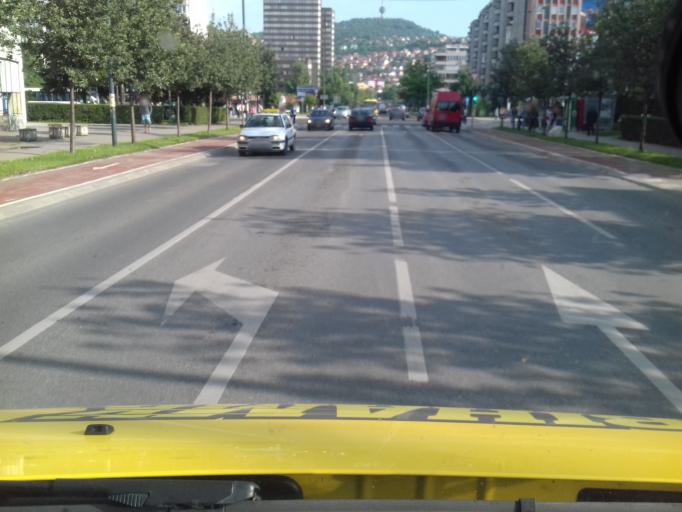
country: BA
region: Federation of Bosnia and Herzegovina
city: Kobilja Glava
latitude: 43.8534
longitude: 18.3928
